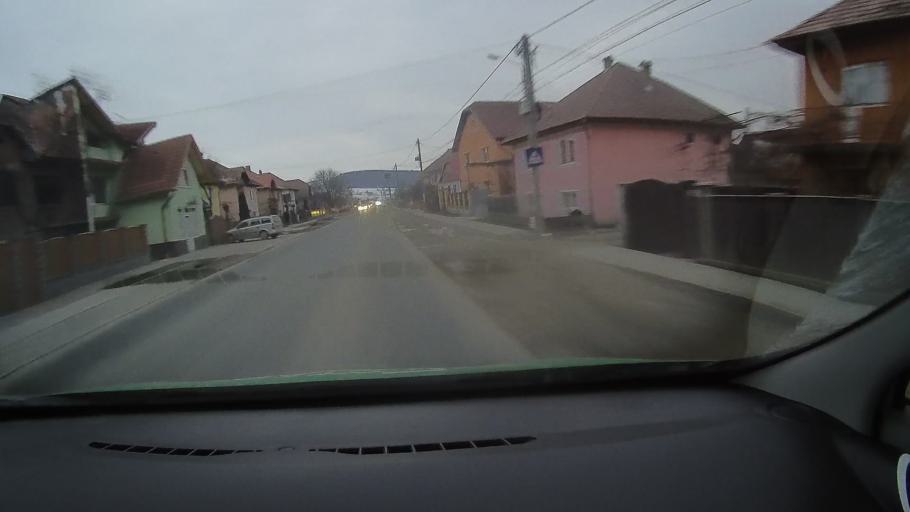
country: RO
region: Harghita
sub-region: Comuna Feliceni
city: Feliceni
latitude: 46.2700
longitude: 25.2750
